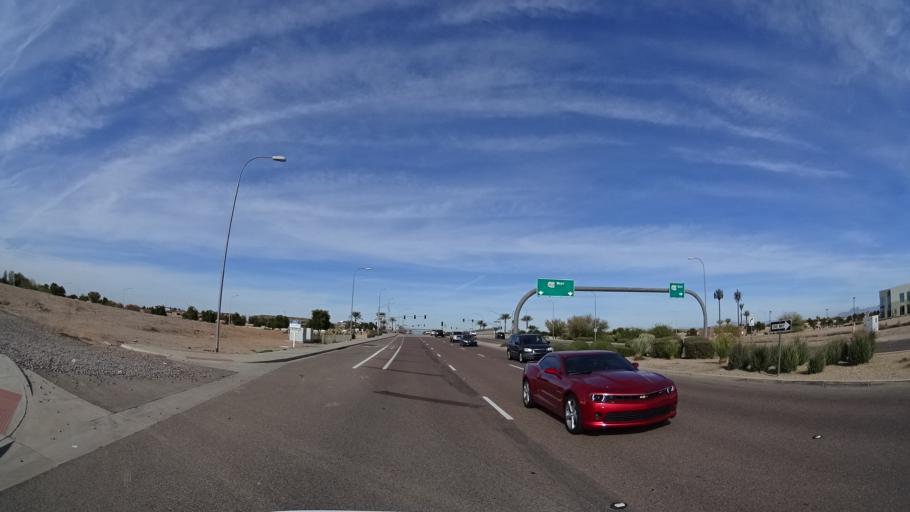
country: US
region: Arizona
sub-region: Maricopa County
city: Chandler
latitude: 33.2809
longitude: -111.8071
